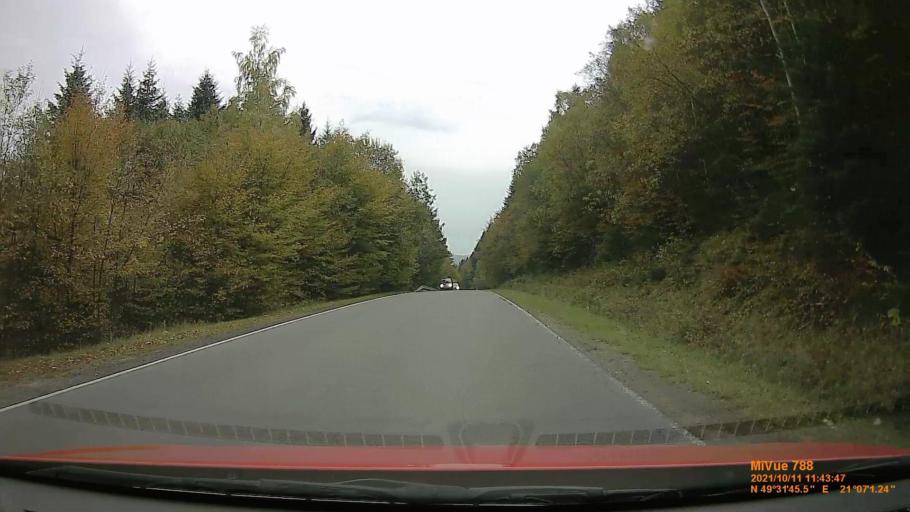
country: PL
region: Lesser Poland Voivodeship
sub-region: Powiat gorlicki
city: Uscie Gorlickie
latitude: 49.5292
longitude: 21.1173
